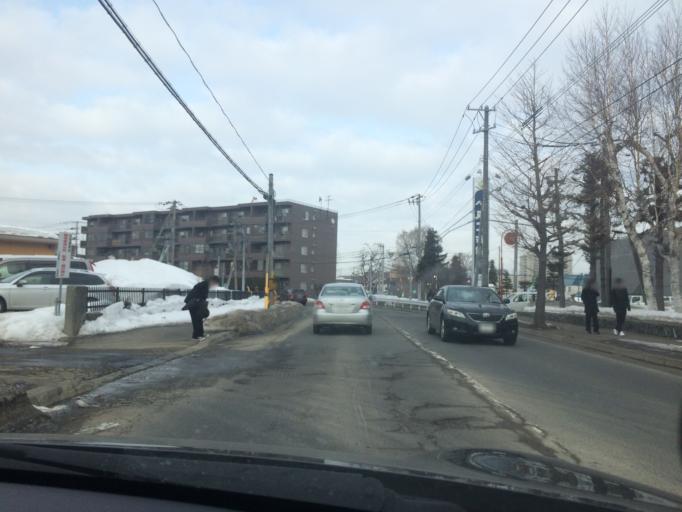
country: JP
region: Hokkaido
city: Sapporo
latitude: 43.0758
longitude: 141.3825
